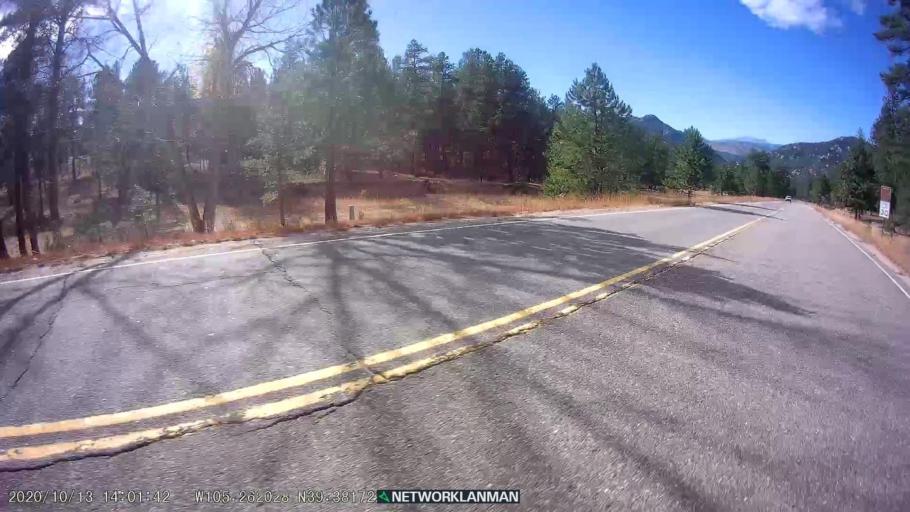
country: US
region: Colorado
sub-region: Douglas County
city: Roxborough Park
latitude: 39.3818
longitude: -105.2621
